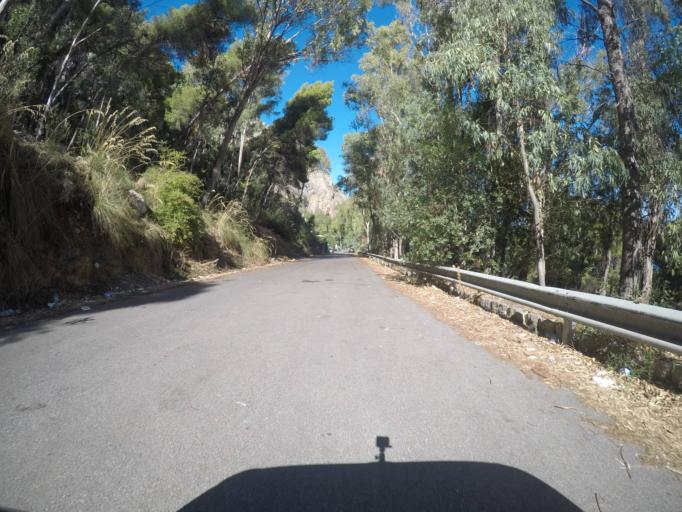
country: IT
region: Sicily
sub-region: Palermo
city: Palermo
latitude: 38.1869
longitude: 13.3434
